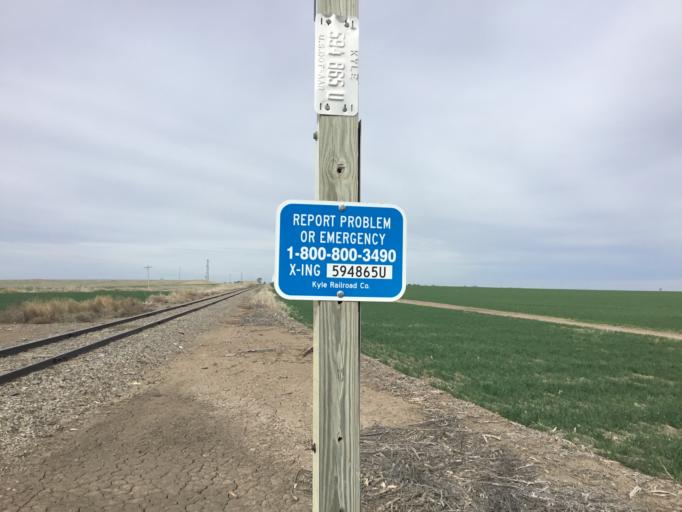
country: US
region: Colorado
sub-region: Kit Carson County
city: Burlington
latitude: 39.3367
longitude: -102.0047
